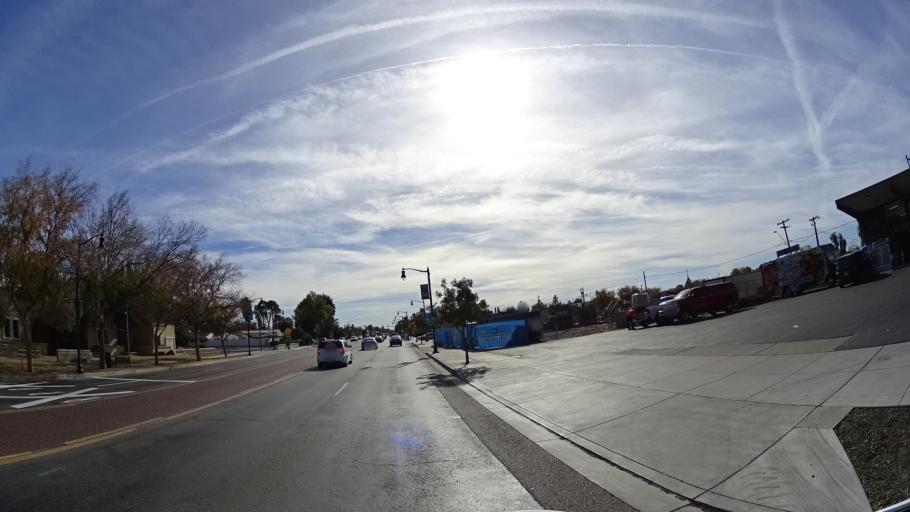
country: US
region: Arizona
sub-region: Maricopa County
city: Gilbert
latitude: 33.3524
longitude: -111.7897
